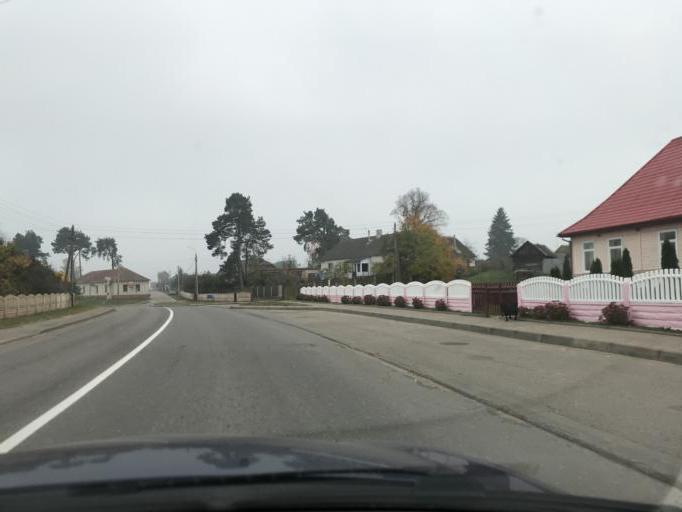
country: BY
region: Grodnenskaya
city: Hrodna
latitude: 53.8152
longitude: 23.8613
